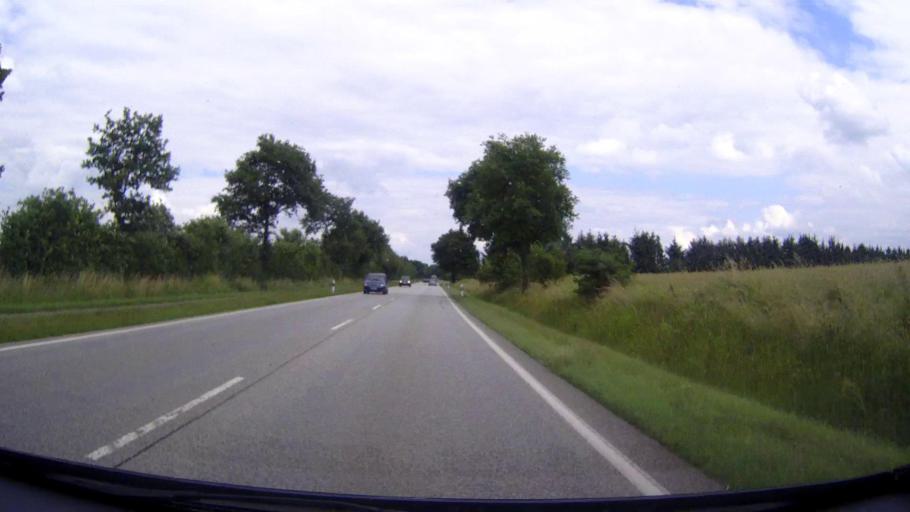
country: DE
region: Schleswig-Holstein
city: Aukrug
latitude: 54.0709
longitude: 9.8200
